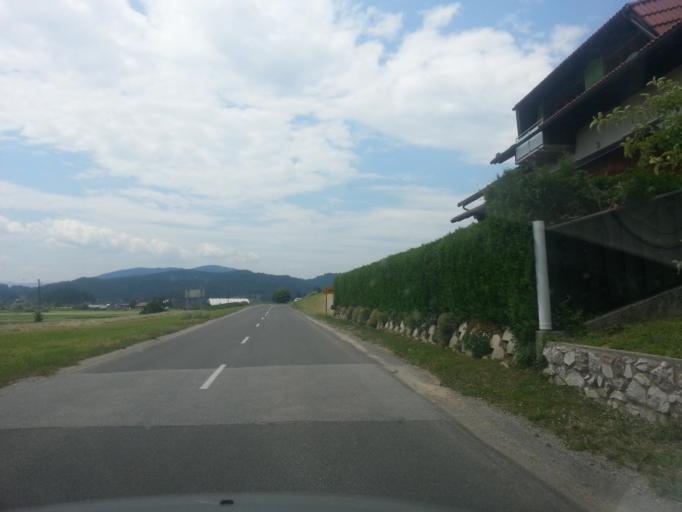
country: SI
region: Horjul
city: Horjul
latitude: 46.0228
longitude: 14.3126
